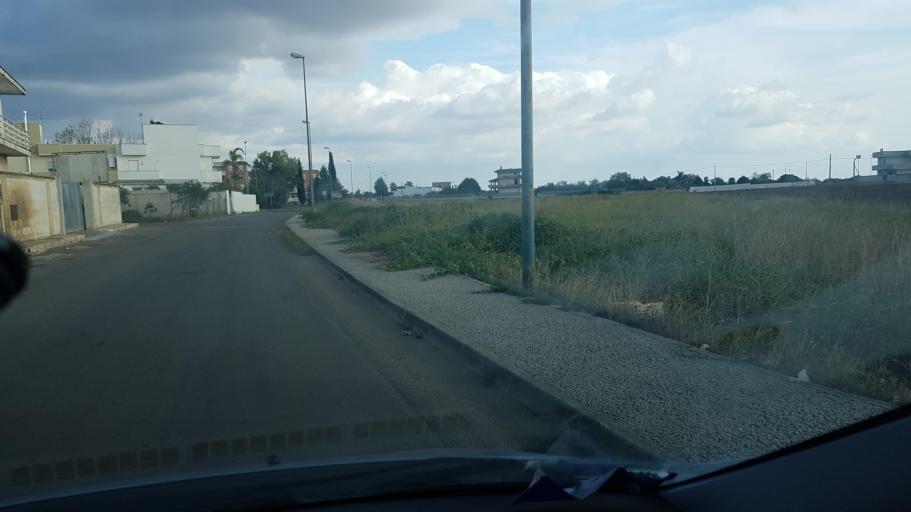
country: IT
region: Apulia
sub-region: Provincia di Brindisi
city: Cellino San Marco
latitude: 40.4695
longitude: 17.9712
